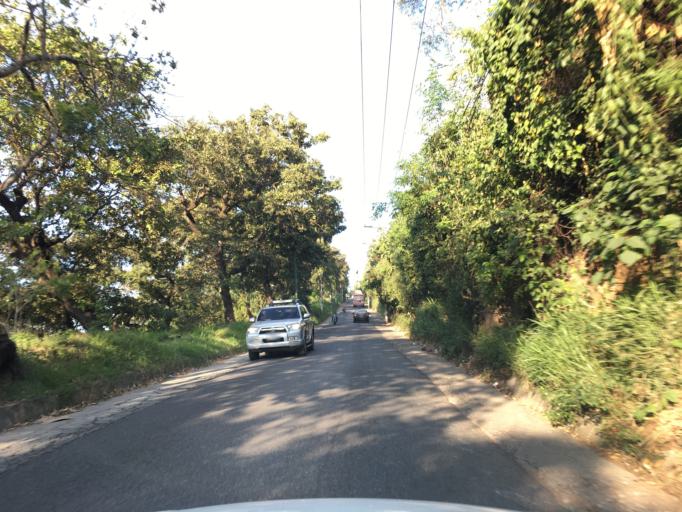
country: GT
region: Guatemala
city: Villa Canales
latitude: 14.4846
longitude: -90.5303
